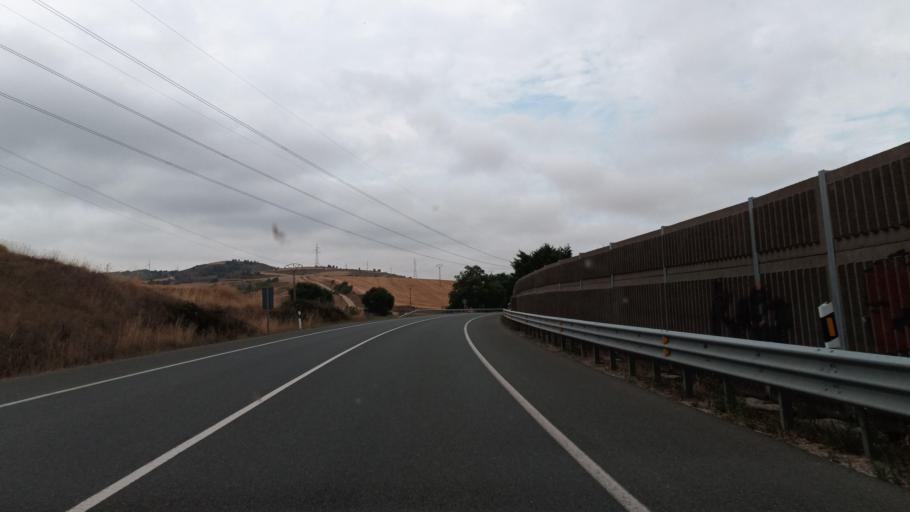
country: ES
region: Castille and Leon
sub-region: Provincia de Burgos
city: Castil de Peones
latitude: 42.4834
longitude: -3.3822
